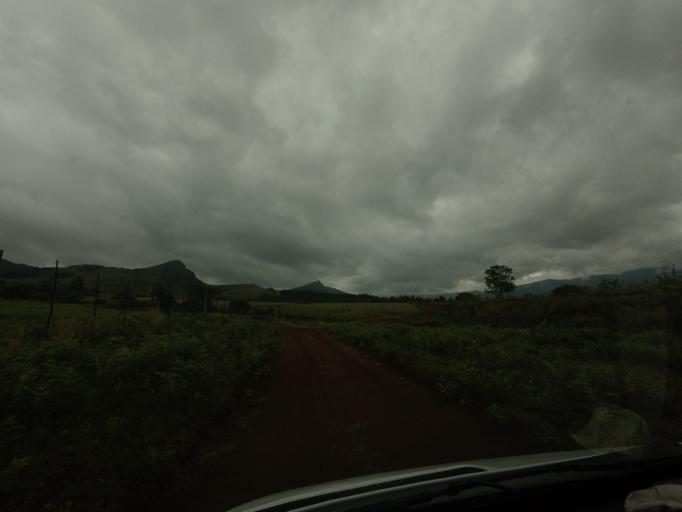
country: SZ
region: Hhohho
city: Lobamba
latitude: -26.4690
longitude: 31.1854
